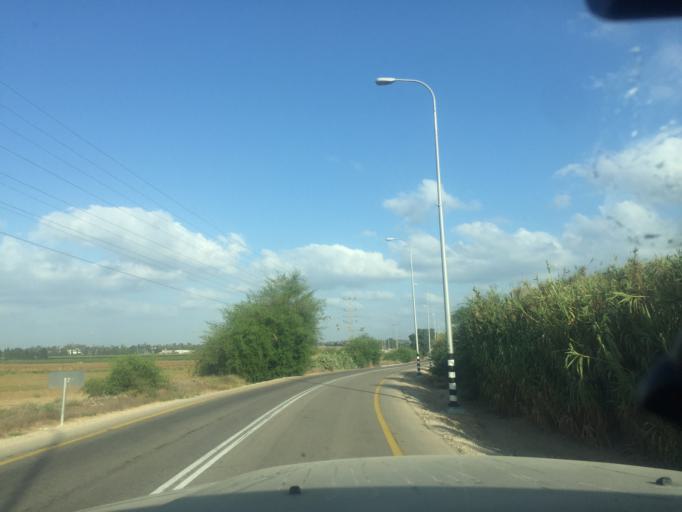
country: PS
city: Umm an Nasr
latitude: 31.6048
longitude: 34.5586
